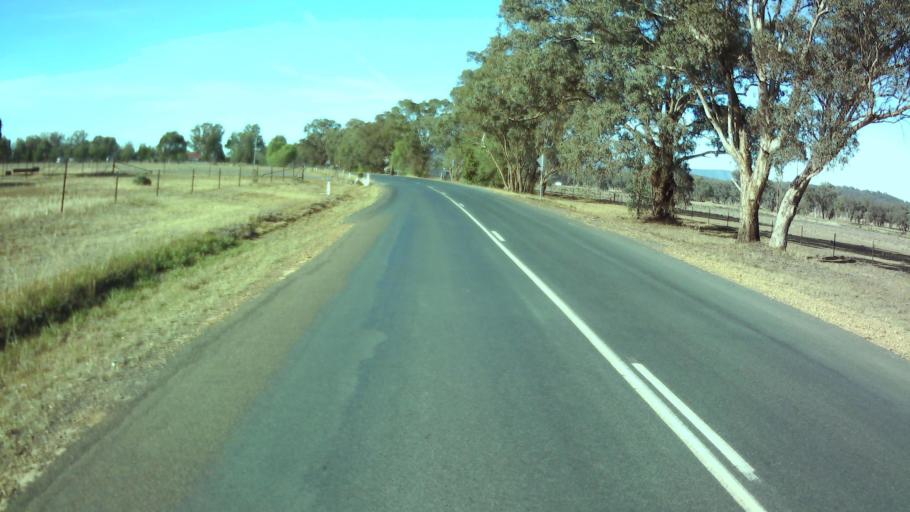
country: AU
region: New South Wales
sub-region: Weddin
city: Grenfell
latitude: -33.9069
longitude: 148.1467
